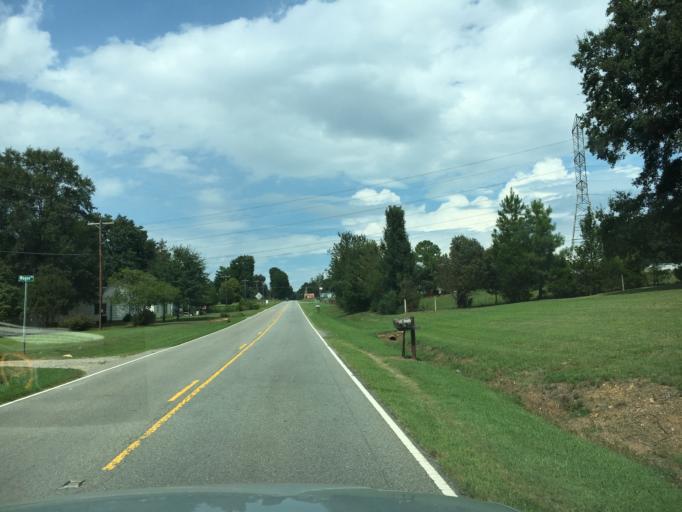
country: US
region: North Carolina
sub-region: Catawba County
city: Maiden
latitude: 35.5386
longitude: -81.2087
